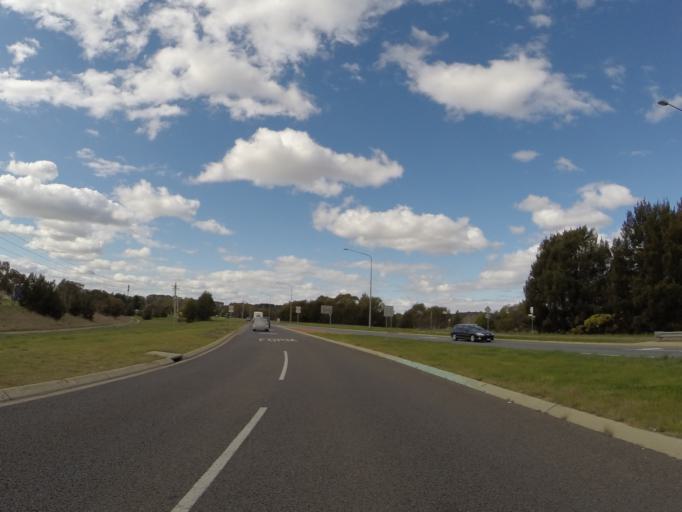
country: AU
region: Australian Capital Territory
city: Belconnen
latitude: -35.2160
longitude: 149.0847
